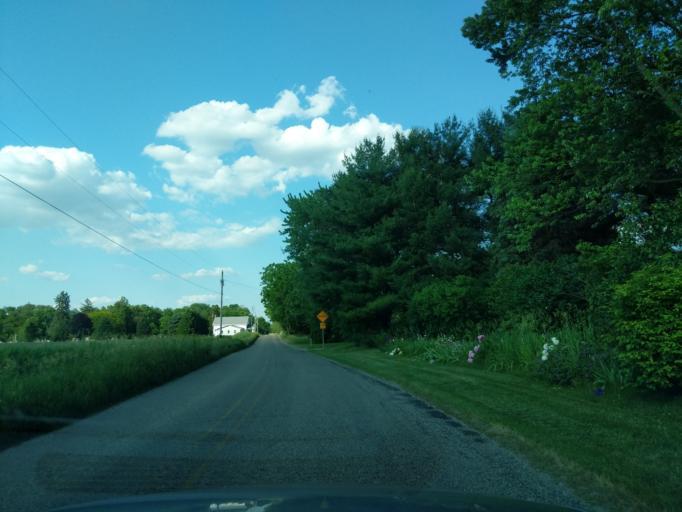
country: US
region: Indiana
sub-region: Kosciusko County
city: North Webster
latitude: 41.3058
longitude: -85.6389
